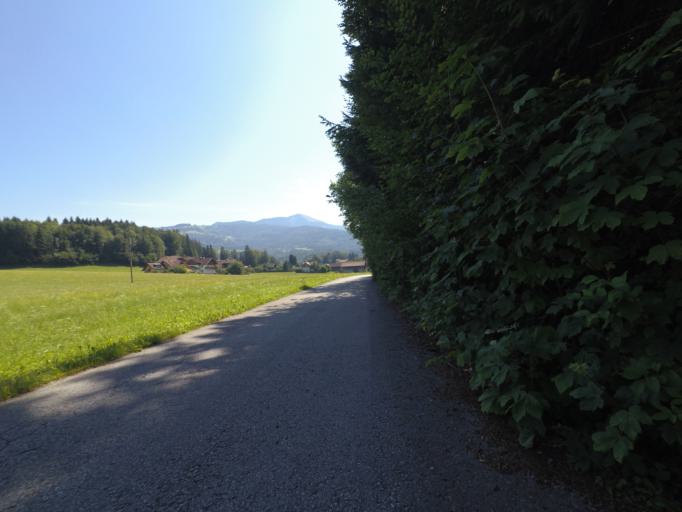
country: AT
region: Salzburg
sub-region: Politischer Bezirk Hallein
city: Adnet
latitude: 47.6800
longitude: 13.1315
